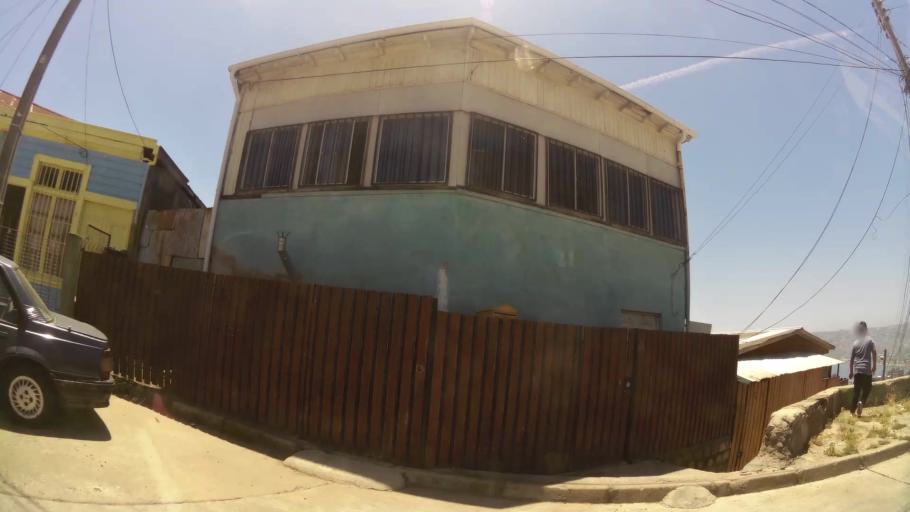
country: CL
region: Valparaiso
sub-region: Provincia de Valparaiso
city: Valparaiso
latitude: -33.0363
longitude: -71.6366
